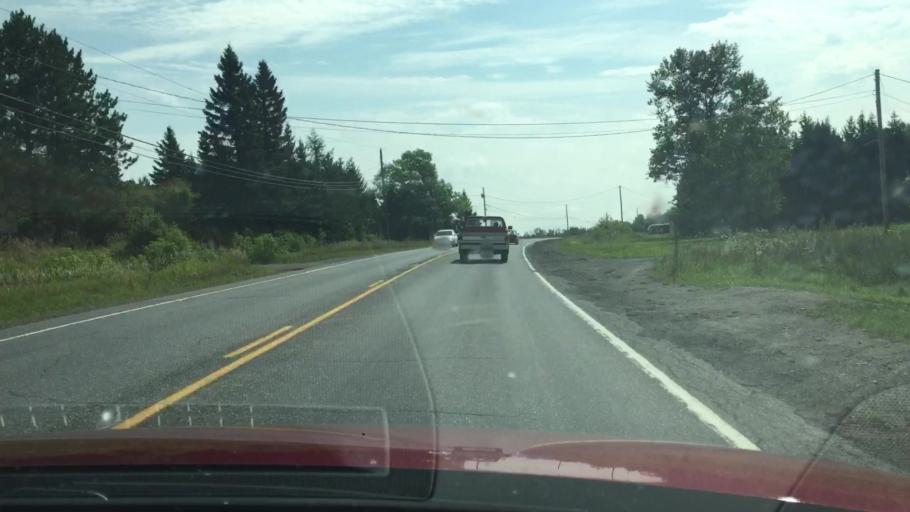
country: US
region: Maine
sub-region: Aroostook County
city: Presque Isle
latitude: 46.6191
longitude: -67.9845
